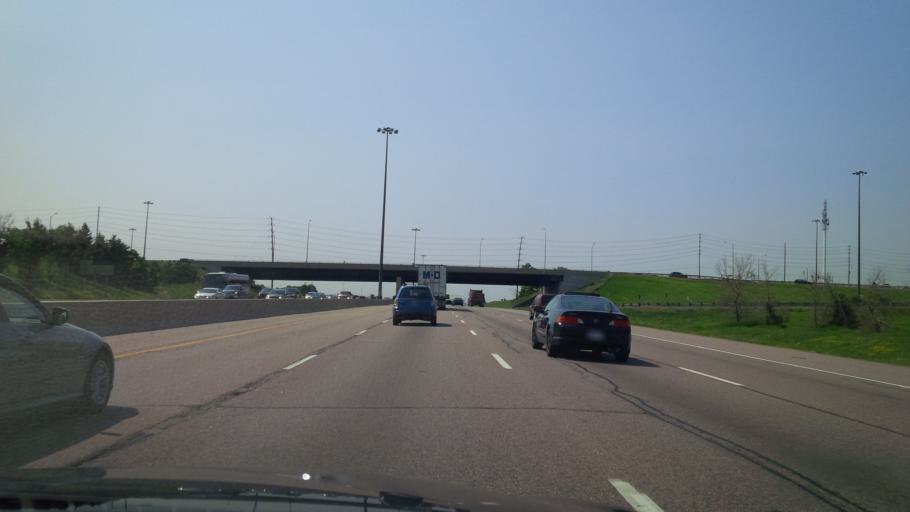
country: CA
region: Ontario
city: Vaughan
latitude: 43.8302
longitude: -79.5467
